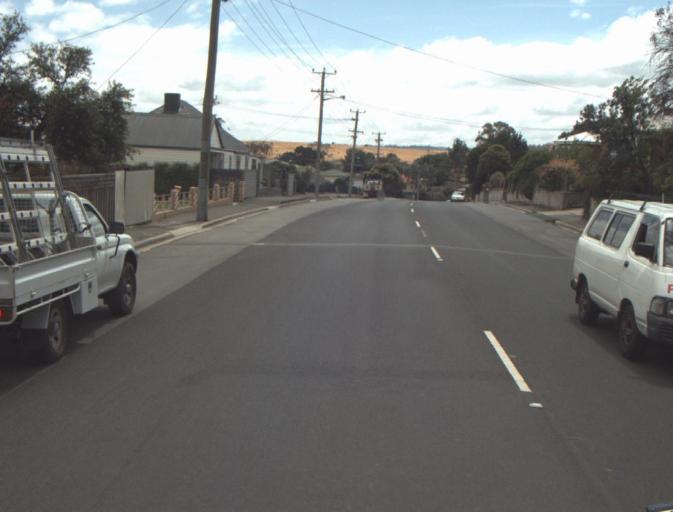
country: AU
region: Tasmania
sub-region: Launceston
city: Newstead
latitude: -41.4571
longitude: 147.2001
